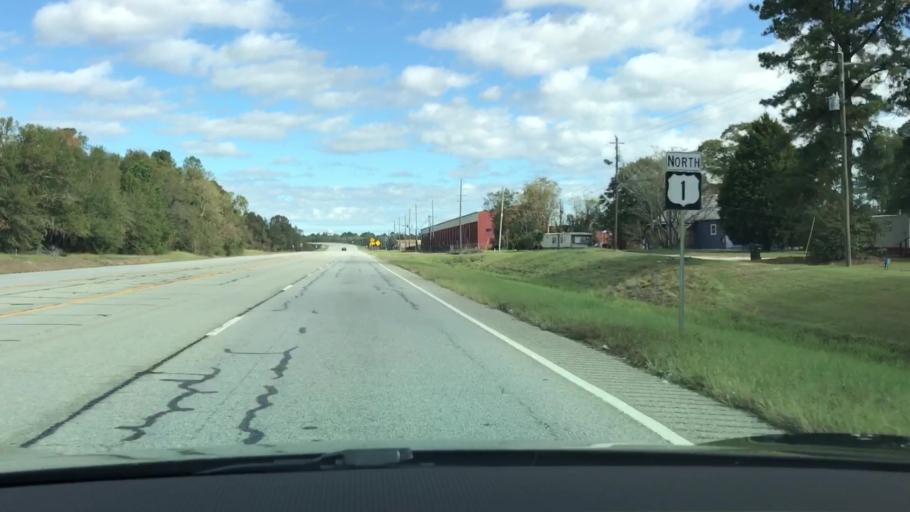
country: US
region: Georgia
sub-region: Jefferson County
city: Wadley
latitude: 32.8528
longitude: -82.3963
